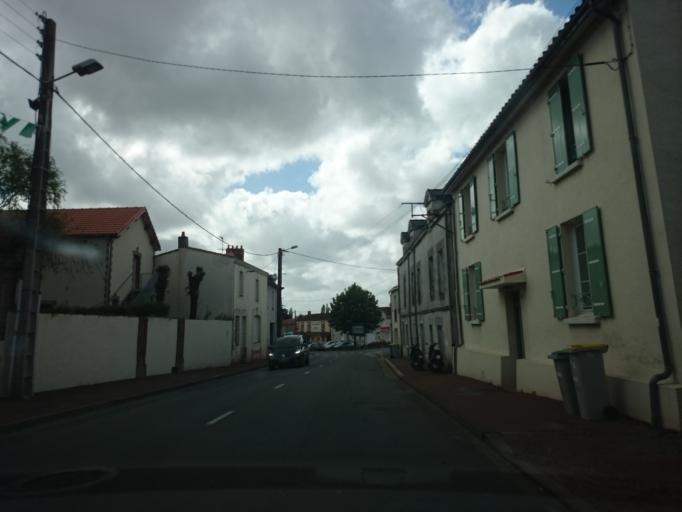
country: FR
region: Pays de la Loire
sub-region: Departement de la Loire-Atlantique
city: Bouaye
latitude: 47.1439
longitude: -1.6943
